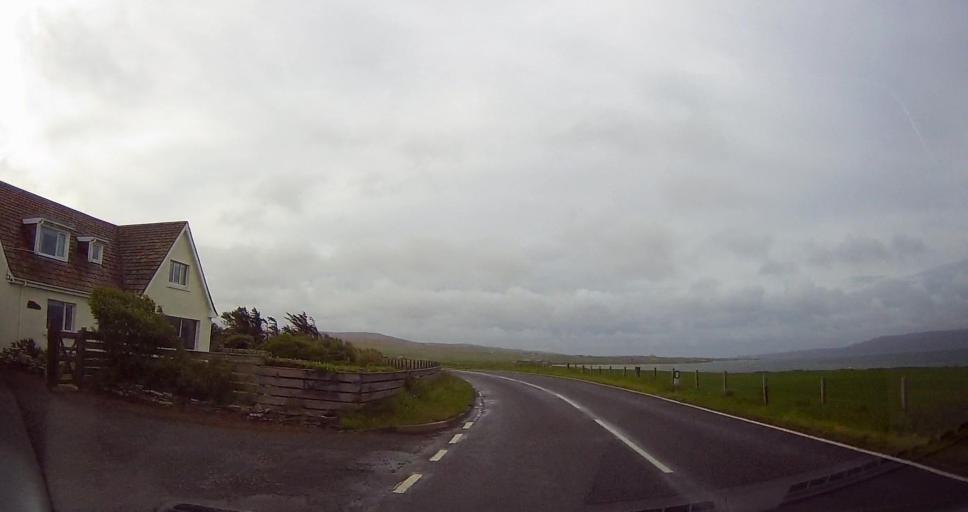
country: GB
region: Scotland
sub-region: Orkney Islands
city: Stromness
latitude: 58.9737
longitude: -3.2388
